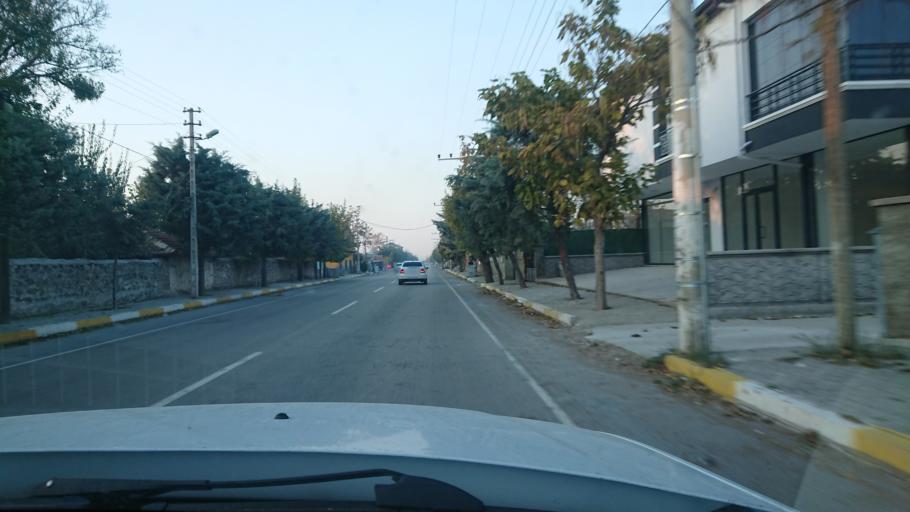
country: TR
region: Aksaray
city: Aksaray
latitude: 38.3025
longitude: 34.0701
